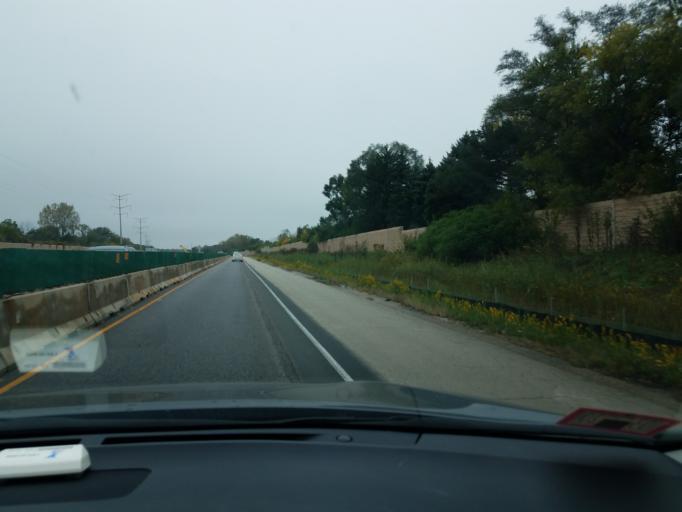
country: US
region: Illinois
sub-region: Cook County
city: Northbrook
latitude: 42.1459
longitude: -87.8078
